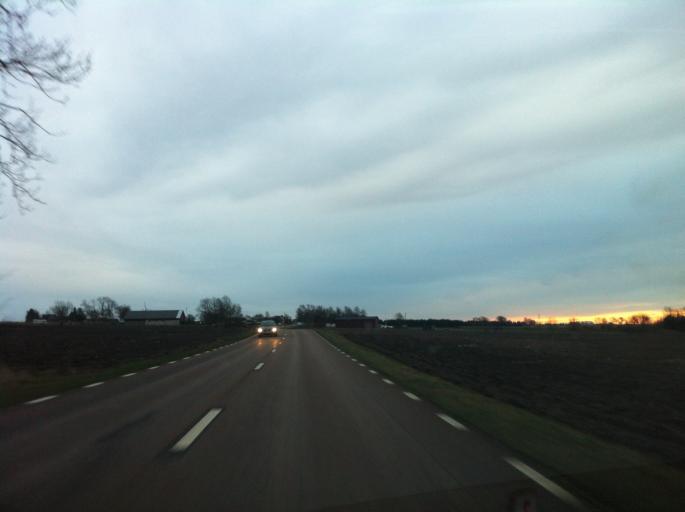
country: SE
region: Skane
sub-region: Landskrona
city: Asmundtorp
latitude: 55.9691
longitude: 12.9414
